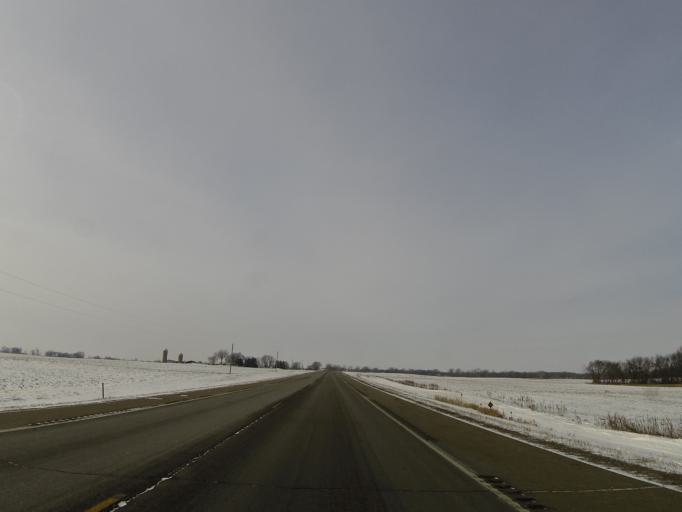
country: US
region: Minnesota
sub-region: Carver County
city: Mayer
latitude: 44.9060
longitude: -93.9556
